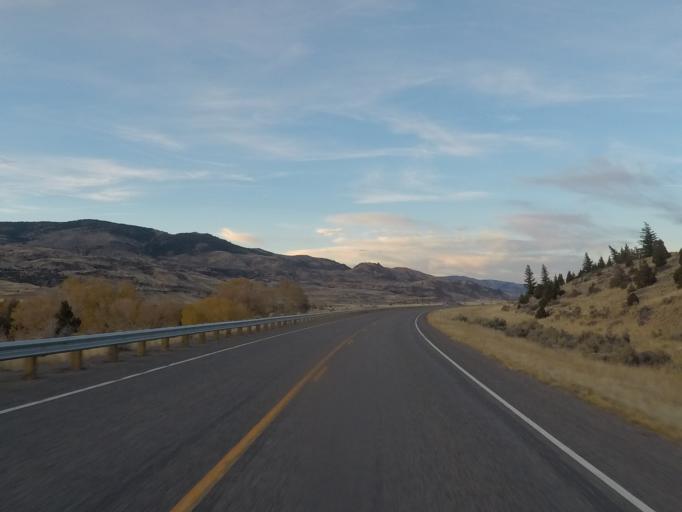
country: US
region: Montana
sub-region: Gallatin County
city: Big Sky
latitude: 45.1979
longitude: -110.9001
